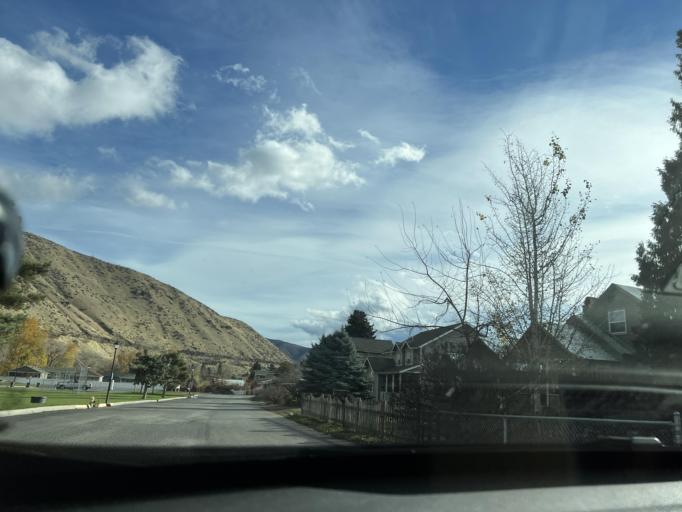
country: US
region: Washington
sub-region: Chelan County
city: Cashmere
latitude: 47.5234
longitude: -120.4667
